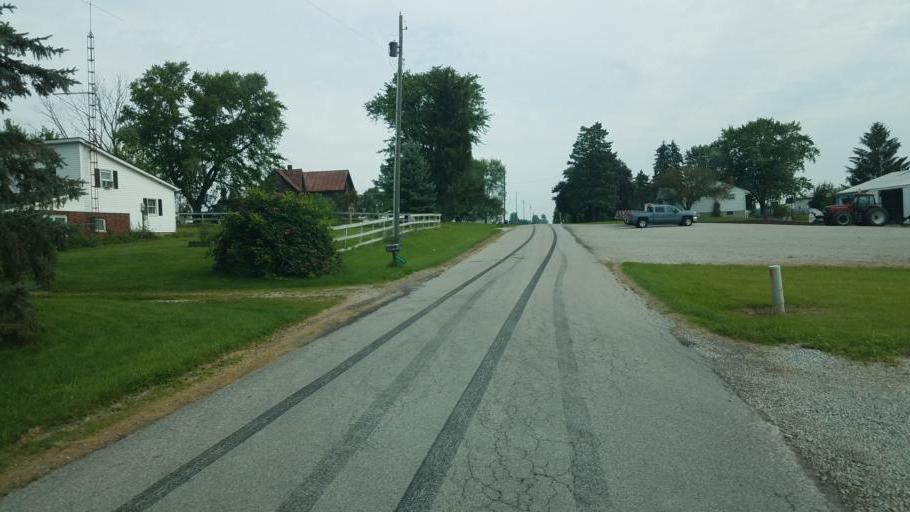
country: US
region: Ohio
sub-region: Morrow County
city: Cardington
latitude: 40.4496
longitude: -82.9058
